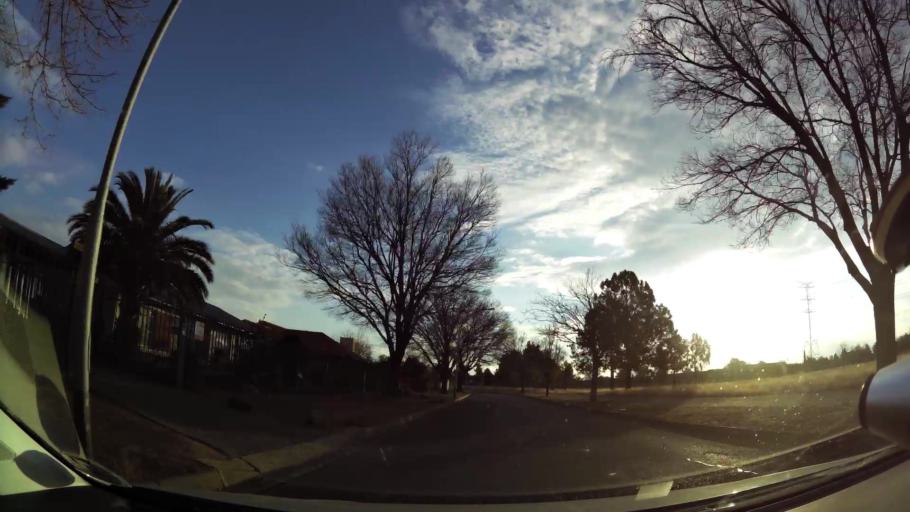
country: ZA
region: Orange Free State
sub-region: Mangaung Metropolitan Municipality
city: Bloemfontein
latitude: -29.1344
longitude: 26.1858
